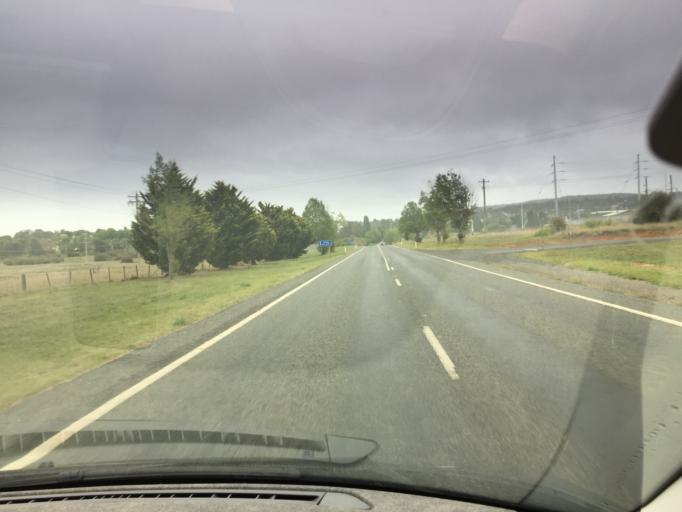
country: AU
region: New South Wales
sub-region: Cooma-Monaro
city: Cooma
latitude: -36.2155
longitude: 149.1452
